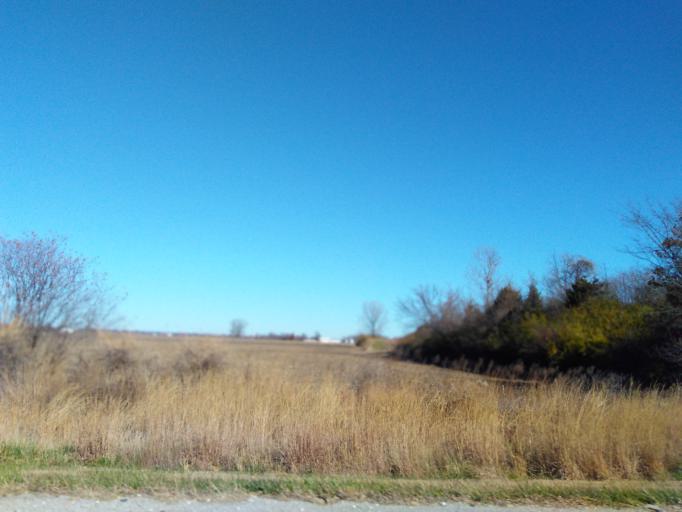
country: US
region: Illinois
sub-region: Saint Clair County
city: Dupo
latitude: 38.4786
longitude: -90.2477
